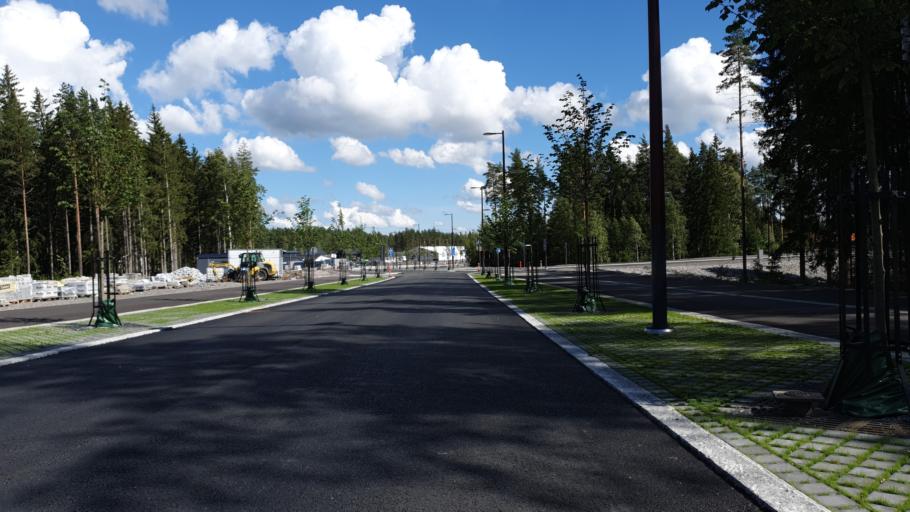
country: FI
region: Uusimaa
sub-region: Helsinki
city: Tuusula
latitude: 60.3983
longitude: 25.0436
